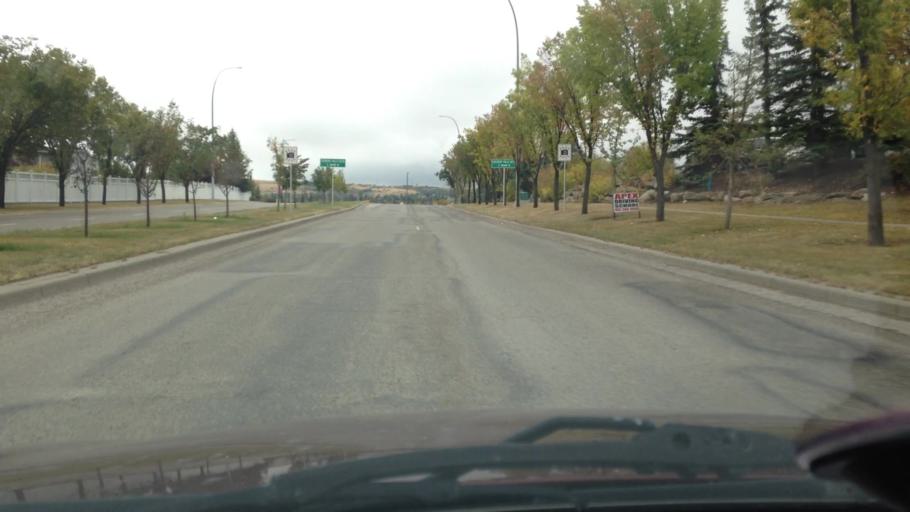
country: CA
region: Alberta
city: Calgary
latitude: 51.1458
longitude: -114.1068
